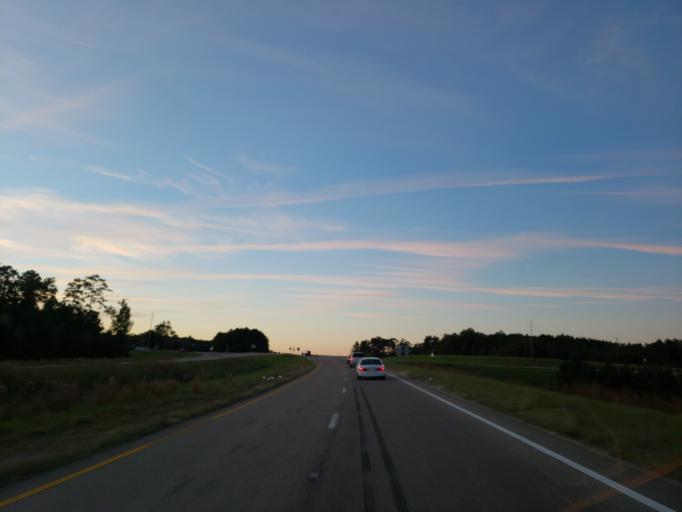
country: US
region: Mississippi
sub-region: Wayne County
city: Waynesboro
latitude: 31.6988
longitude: -88.6191
